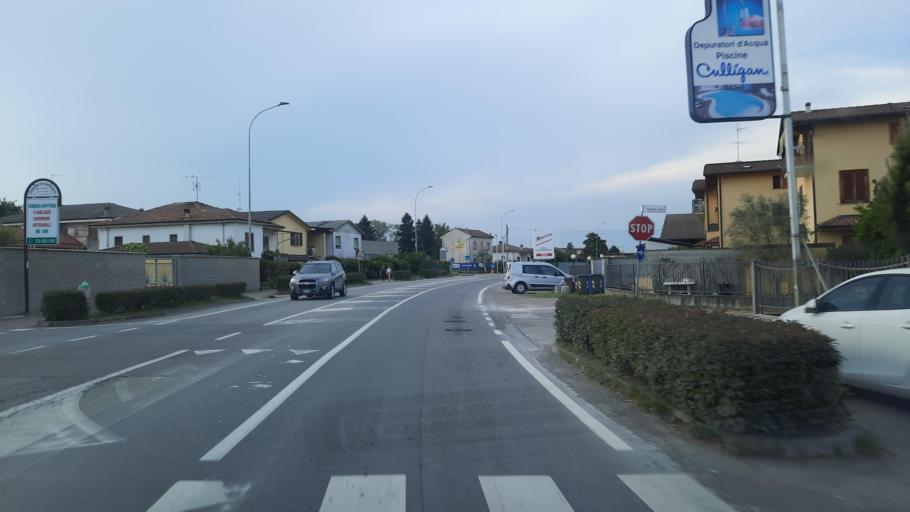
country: IT
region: Lombardy
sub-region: Provincia di Pavia
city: Garlasco
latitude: 45.1936
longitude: 8.9140
